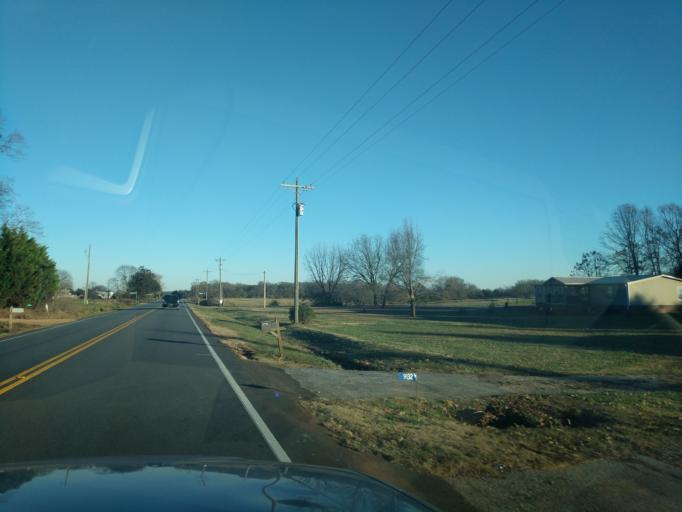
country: US
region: South Carolina
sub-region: Oconee County
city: Utica
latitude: 34.5933
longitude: -82.9677
